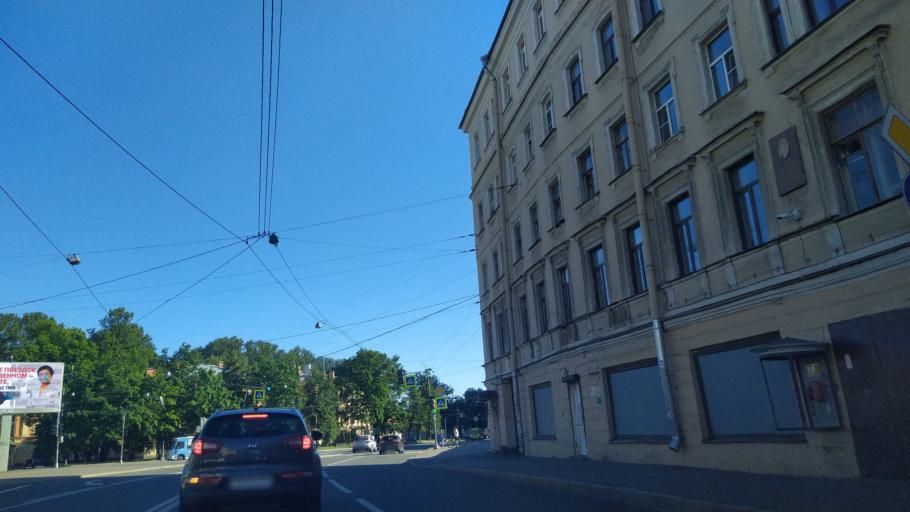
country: RU
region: Leningrad
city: Finlyandskiy
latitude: 59.9599
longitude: 30.3454
